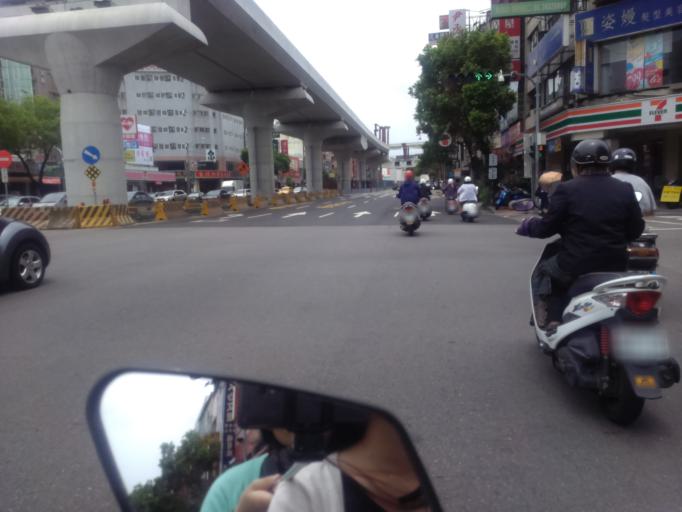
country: TW
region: Taiwan
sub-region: Taichung City
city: Taichung
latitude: 24.1658
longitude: 120.6521
